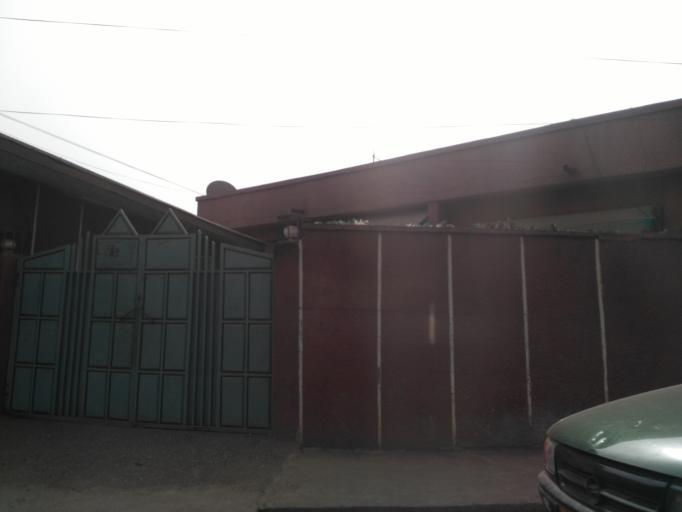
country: GH
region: Ashanti
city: Kumasi
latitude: 6.7032
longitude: -1.6041
